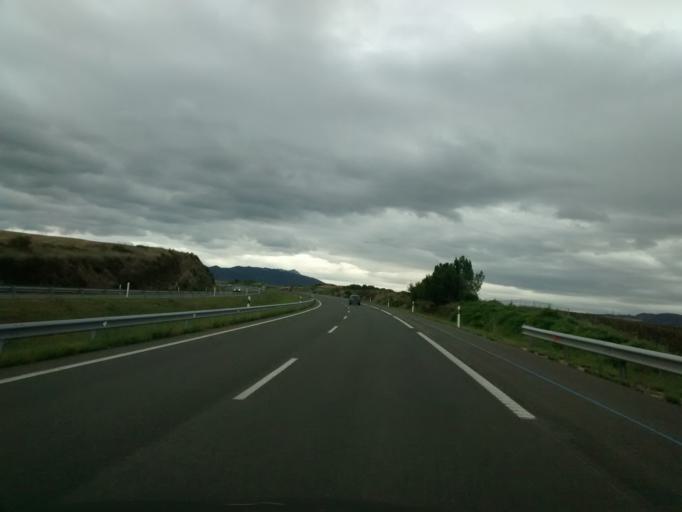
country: ES
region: Castille and Leon
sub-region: Provincia de Burgos
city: Miranda de Ebro
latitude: 42.7231
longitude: -2.9205
